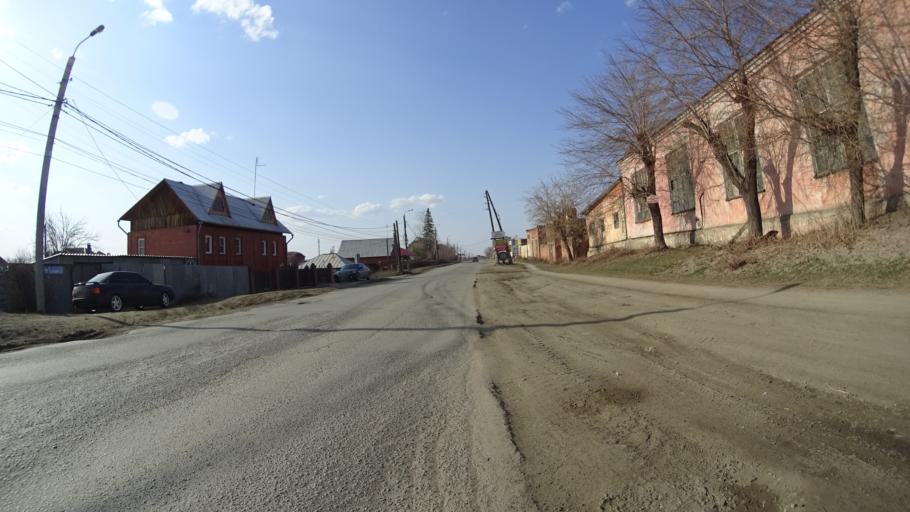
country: RU
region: Chelyabinsk
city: Novosineglazovskiy
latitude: 55.1074
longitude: 61.3356
